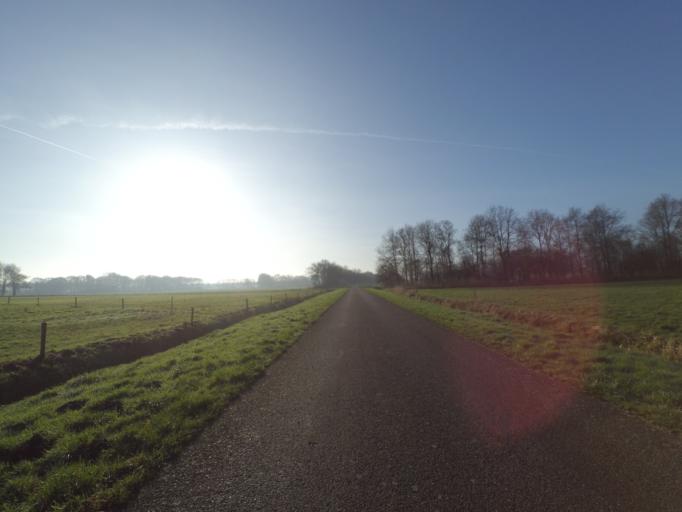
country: NL
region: Drenthe
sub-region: Gemeente Assen
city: Assen
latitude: 52.8569
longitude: 6.6411
